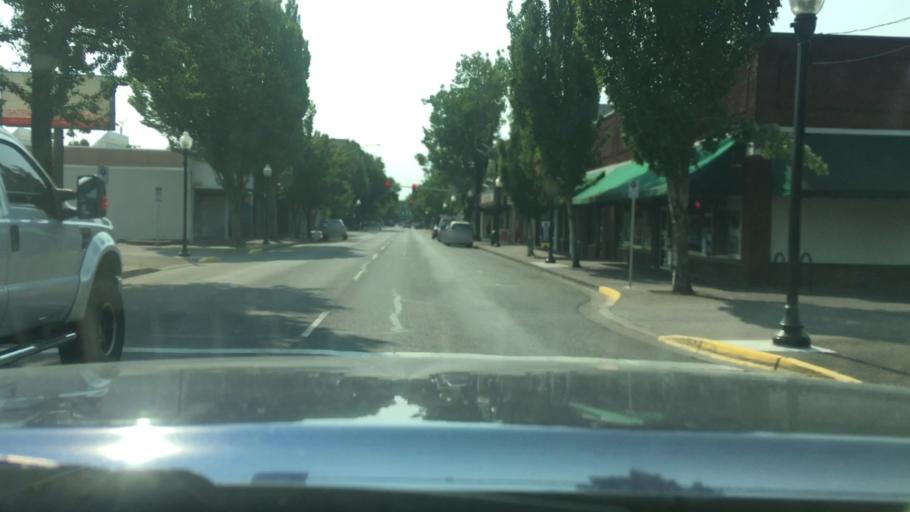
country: US
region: Oregon
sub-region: Lane County
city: Springfield
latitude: 44.0462
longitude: -123.0169
